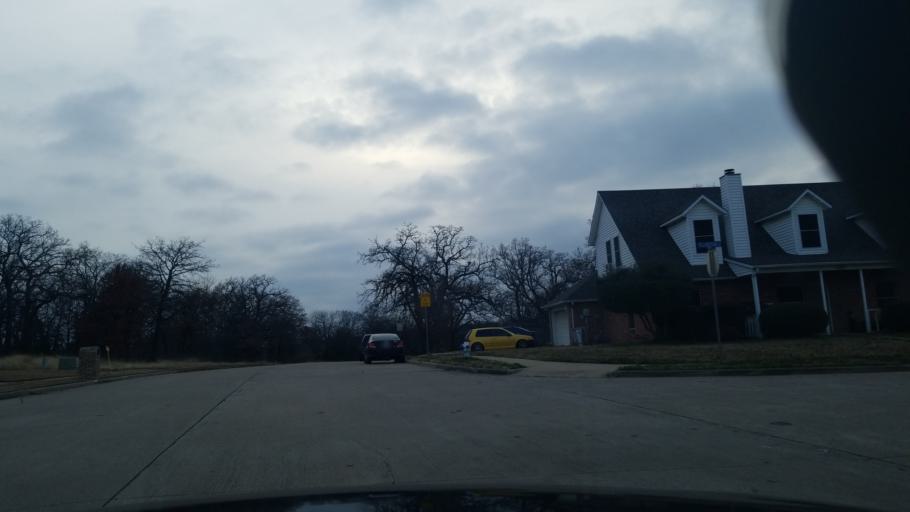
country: US
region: Texas
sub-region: Denton County
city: Corinth
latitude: 33.1366
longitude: -97.0788
